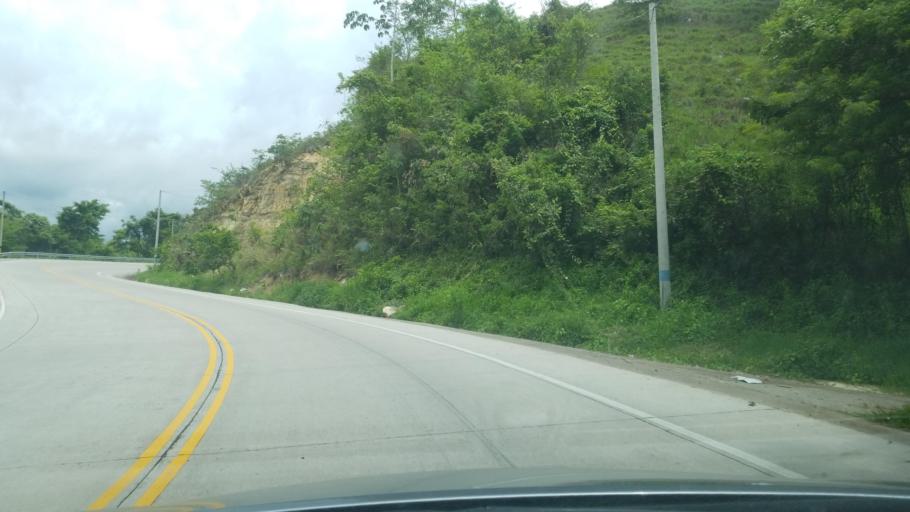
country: HN
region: Copan
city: Florida
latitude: 14.9983
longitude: -88.8455
